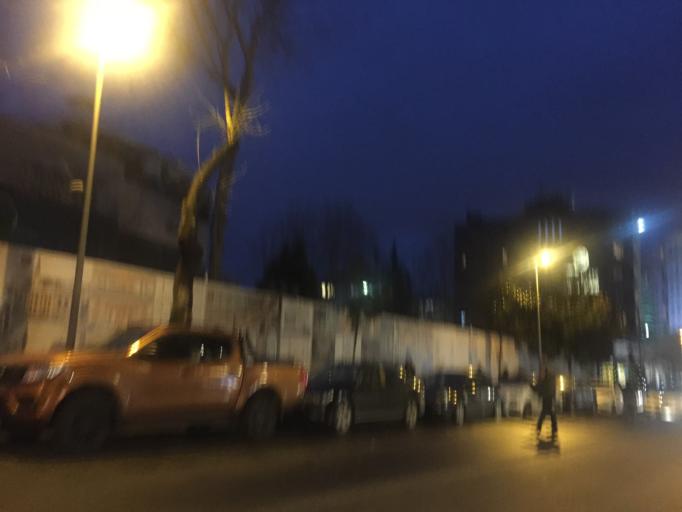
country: TR
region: Istanbul
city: Sisli
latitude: 41.0493
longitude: 28.9939
